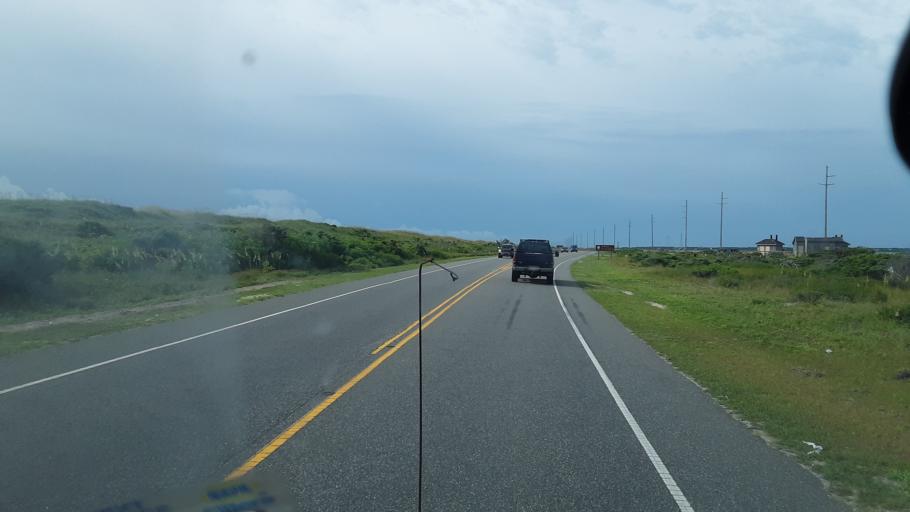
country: US
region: North Carolina
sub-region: Dare County
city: Buxton
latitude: 35.3008
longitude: -75.5129
